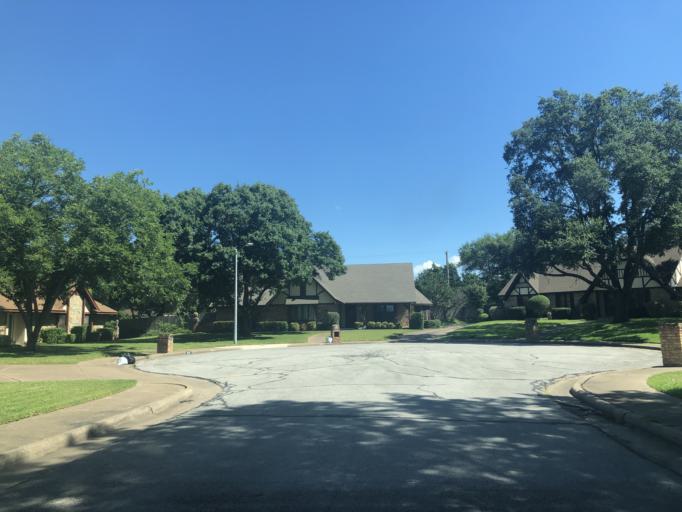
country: US
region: Texas
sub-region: Dallas County
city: Duncanville
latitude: 32.6463
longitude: -96.9382
